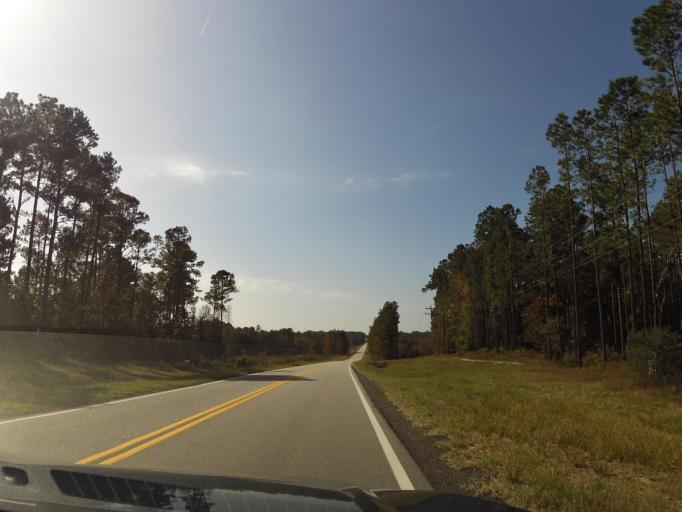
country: US
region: Georgia
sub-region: Charlton County
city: Folkston
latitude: 30.8116
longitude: -82.0198
